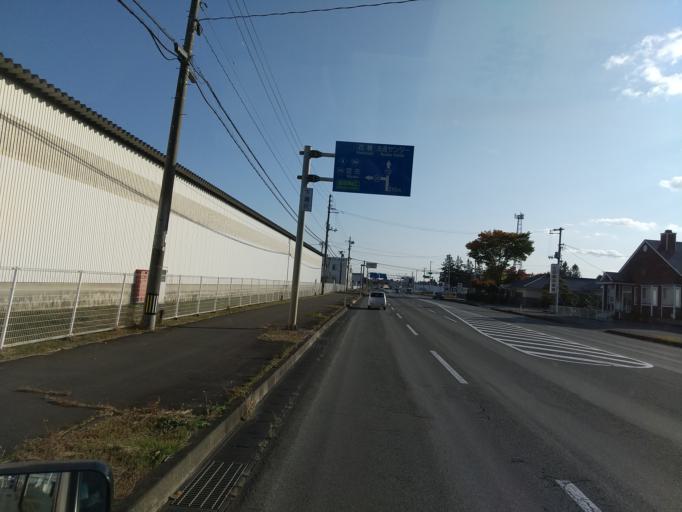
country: JP
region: Iwate
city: Morioka-shi
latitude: 39.6540
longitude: 141.1140
